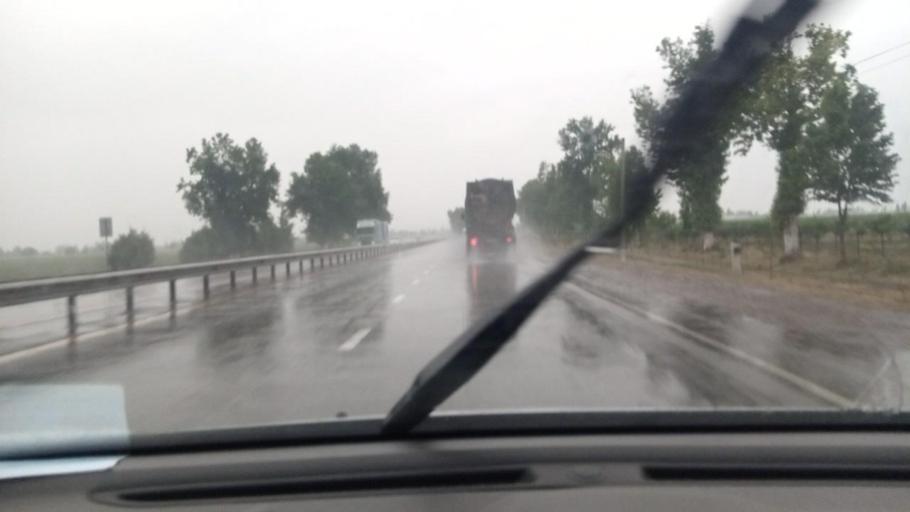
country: UZ
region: Toshkent Shahri
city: Bektemir
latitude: 41.1466
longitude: 69.4301
